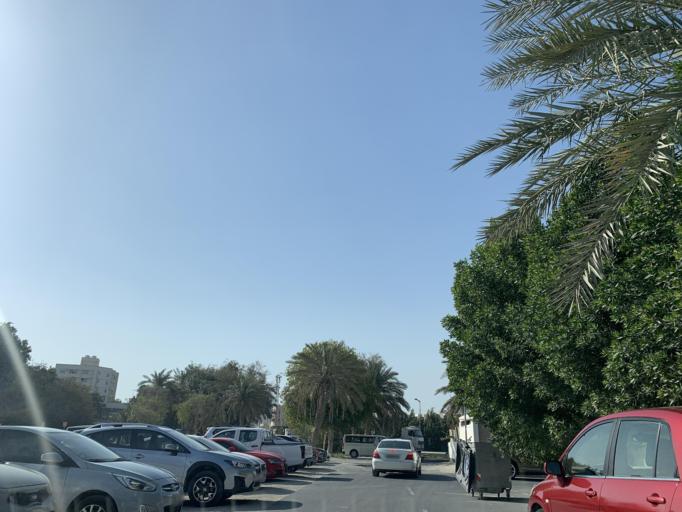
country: BH
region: Manama
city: Manama
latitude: 26.2048
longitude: 50.5902
